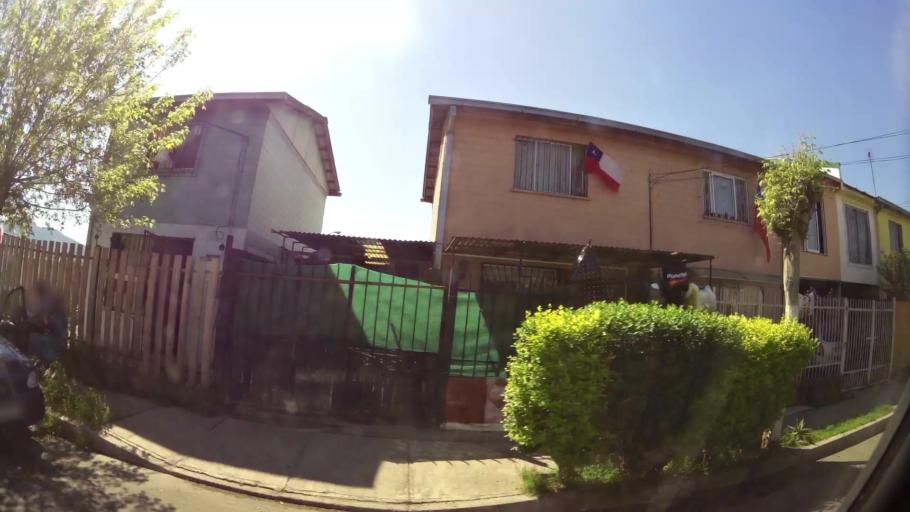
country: CL
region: Santiago Metropolitan
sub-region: Provincia de Talagante
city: Penaflor
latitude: -33.6075
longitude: -70.8809
